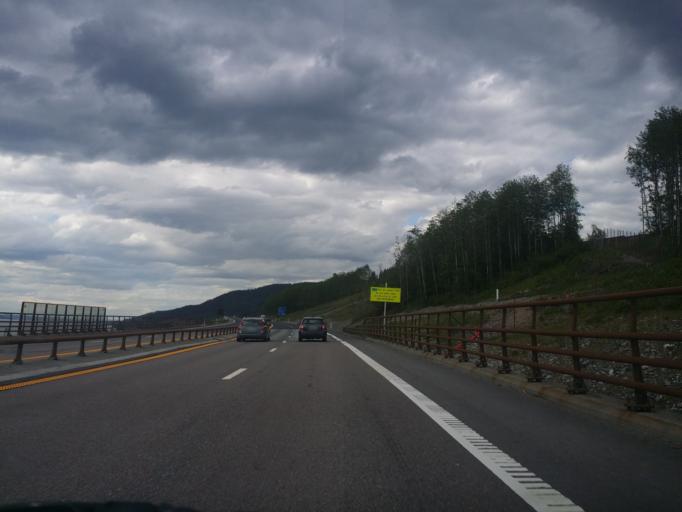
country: NO
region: Akershus
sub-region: Eidsvoll
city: Eidsvoll
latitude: 60.4029
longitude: 11.2366
